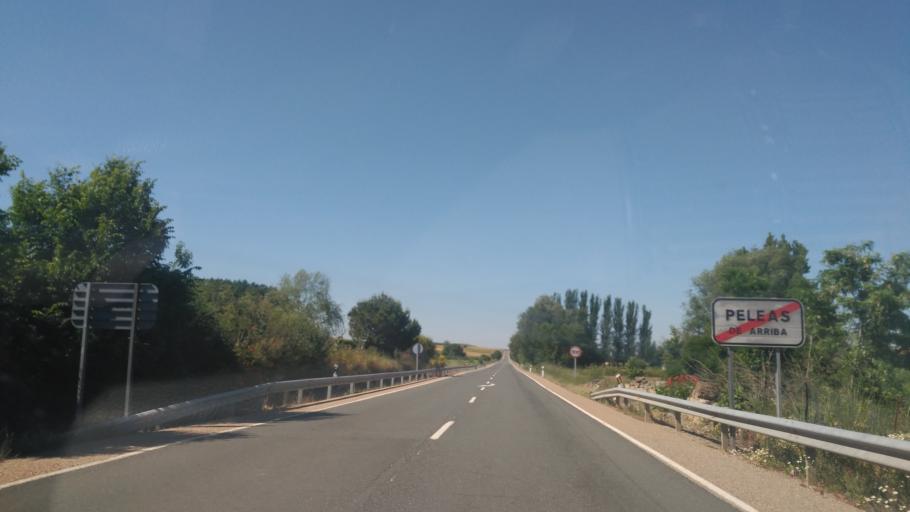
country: ES
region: Castille and Leon
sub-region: Provincia de Zamora
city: Corrales
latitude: 41.3235
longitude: -5.7343
